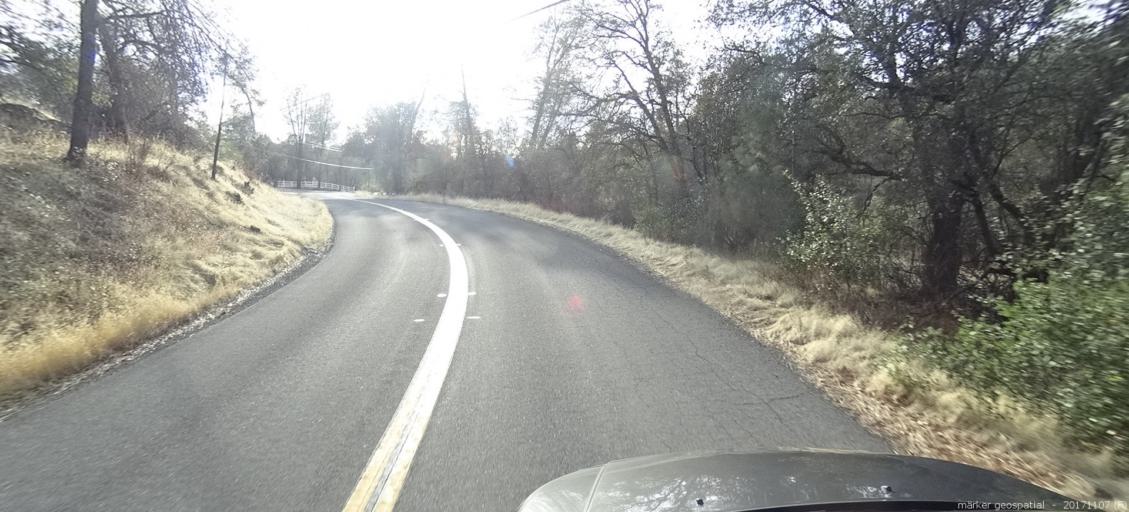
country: US
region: California
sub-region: Shasta County
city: Shasta
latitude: 40.5179
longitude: -122.4633
